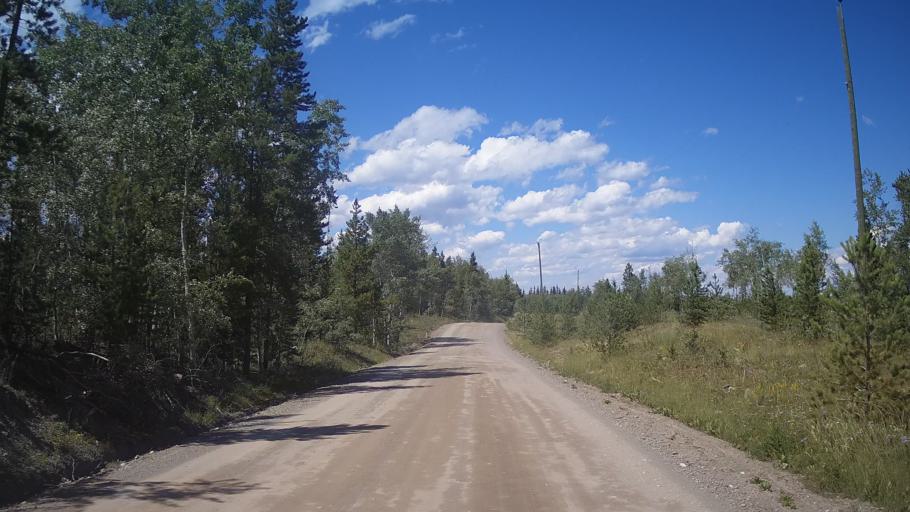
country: CA
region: British Columbia
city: Cache Creek
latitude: 51.2549
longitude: -121.6776
